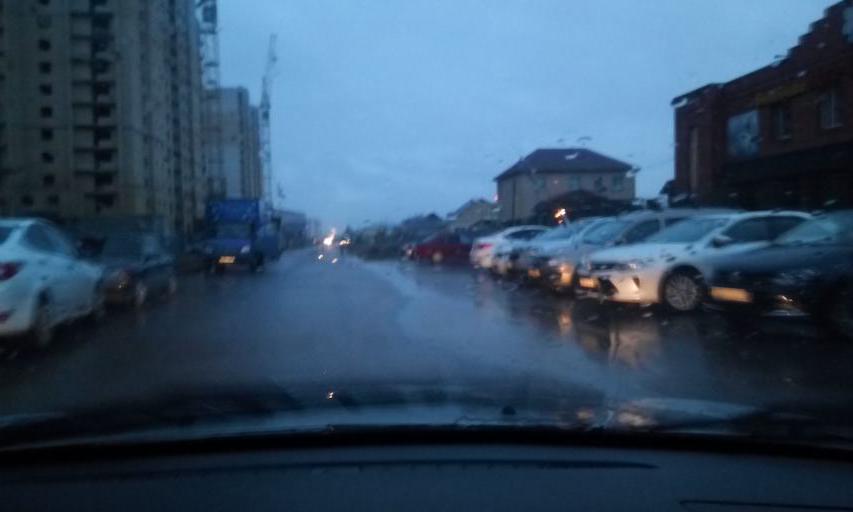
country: KZ
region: Astana Qalasy
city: Astana
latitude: 51.1914
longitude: 71.3402
